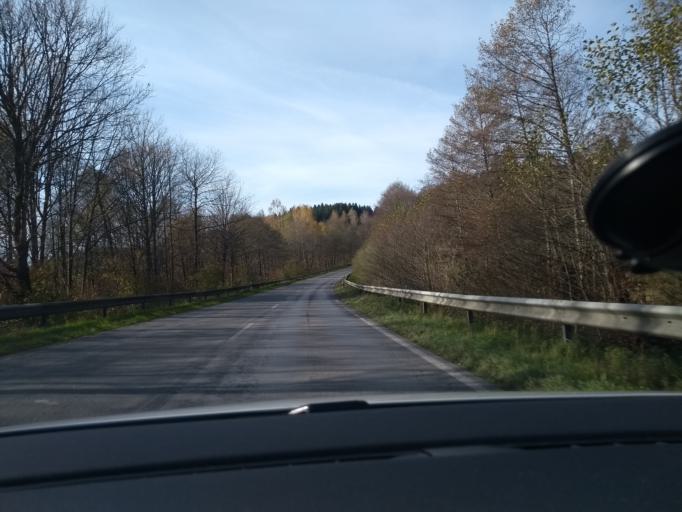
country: DE
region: Bavaria
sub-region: Upper Bavaria
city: Bad Endorf
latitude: 47.9005
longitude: 12.2636
